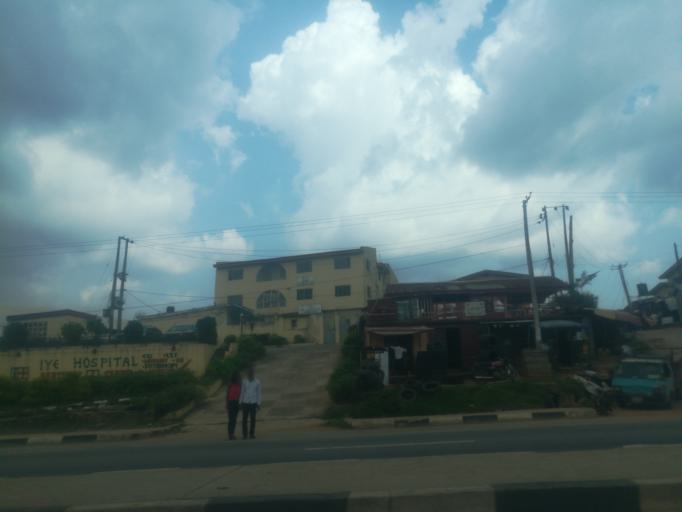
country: NG
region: Oyo
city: Ibadan
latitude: 7.3416
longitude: 3.8774
